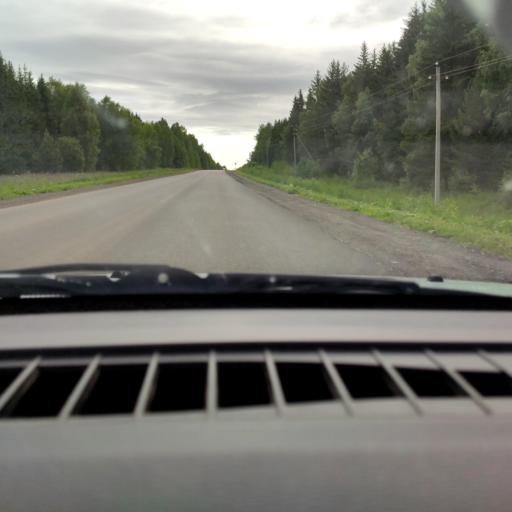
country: RU
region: Perm
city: Orda
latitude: 57.2217
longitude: 56.9522
